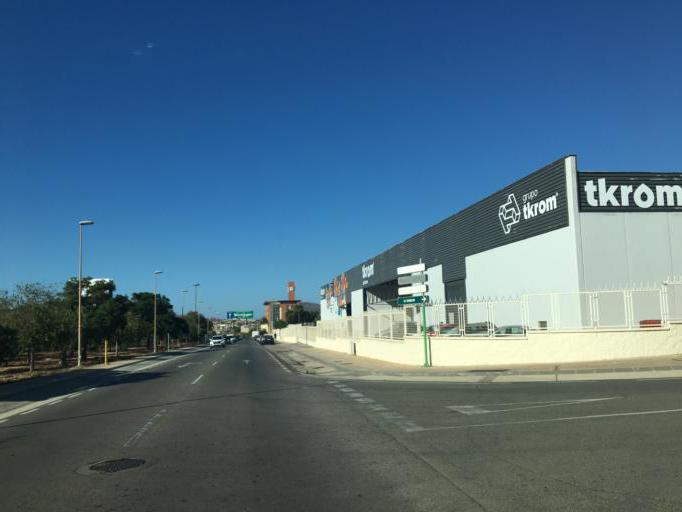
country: ES
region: Murcia
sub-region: Murcia
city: Cartagena
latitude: 37.6193
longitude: -0.9527
